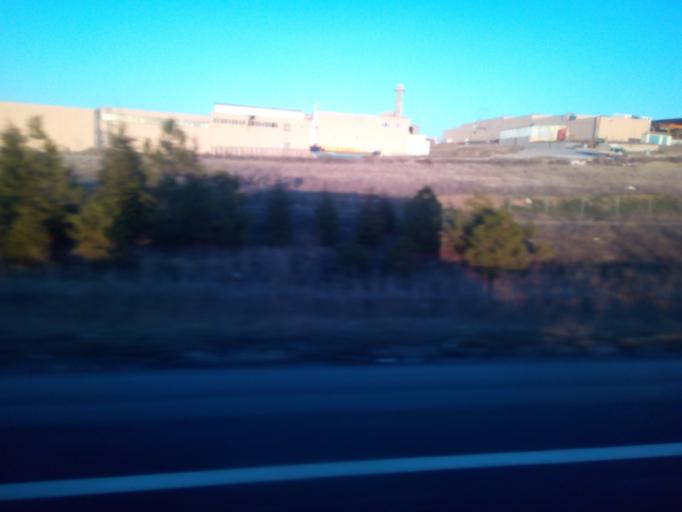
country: TR
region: Ankara
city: Etimesgut
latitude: 40.0437
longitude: 32.5923
